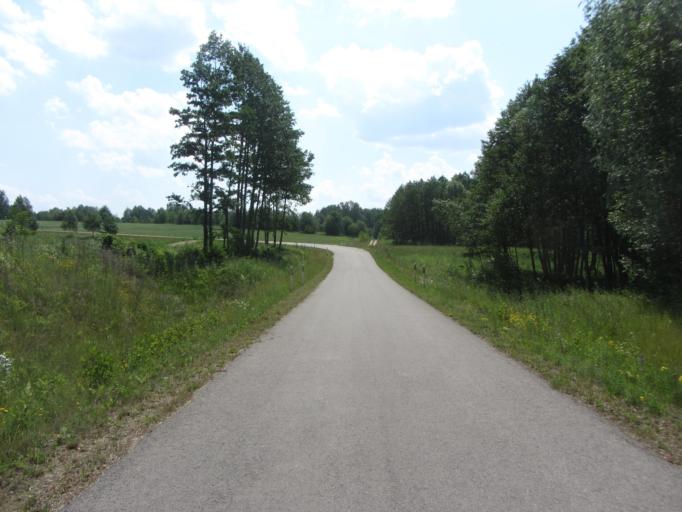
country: LT
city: Lazdijai
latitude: 54.1855
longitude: 23.4276
